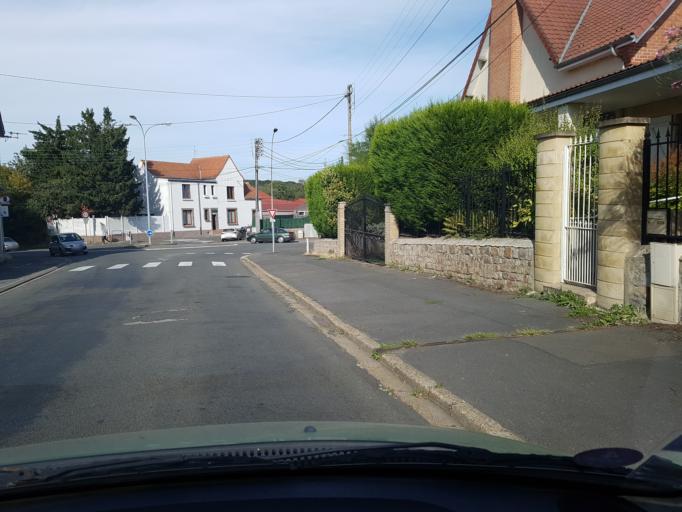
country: FR
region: Nord-Pas-de-Calais
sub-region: Departement du Pas-de-Calais
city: Marles-les-Mines
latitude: 50.4912
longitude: 2.5260
